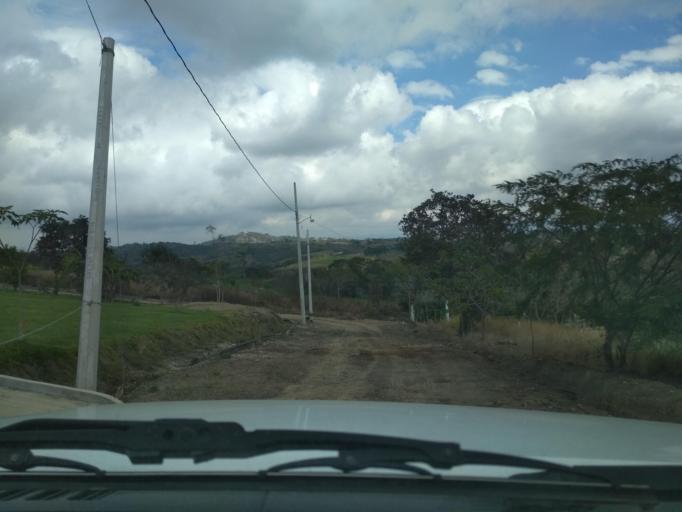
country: MX
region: Veracruz
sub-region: Emiliano Zapata
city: Dos Rios
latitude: 19.5030
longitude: -96.8217
